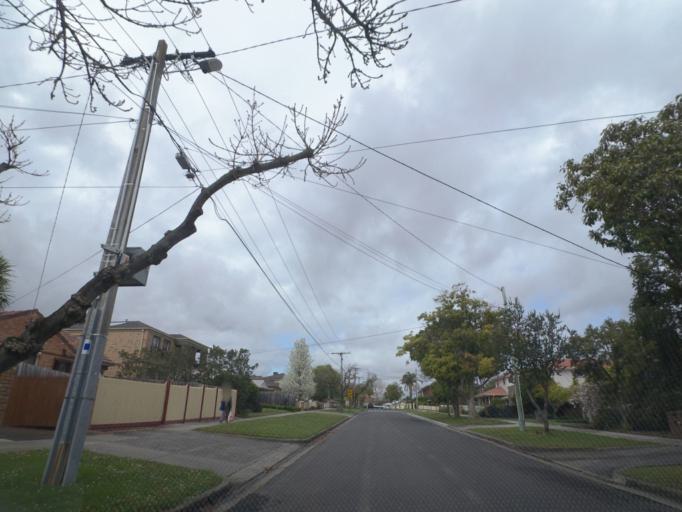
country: AU
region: Victoria
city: Mitcham
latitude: -37.8129
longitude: 145.1894
